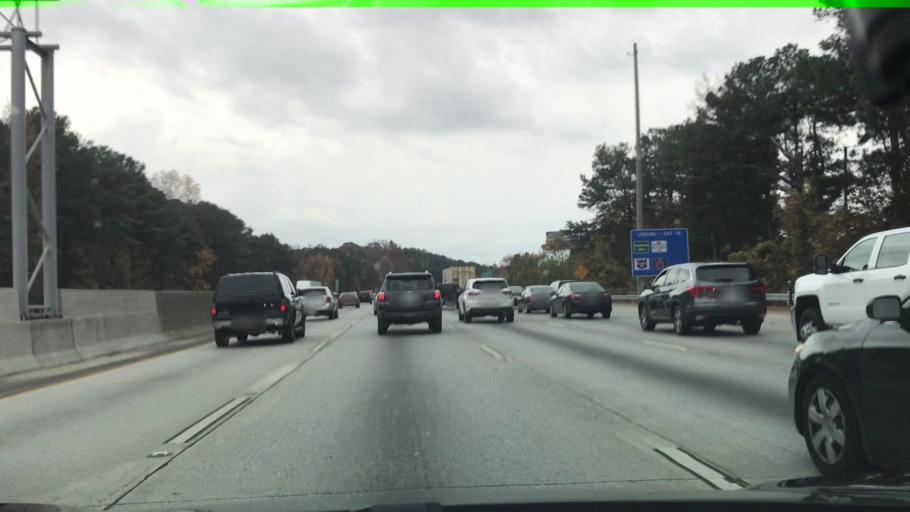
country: US
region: Georgia
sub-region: DeKalb County
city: Clarkston
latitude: 33.8415
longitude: -84.2479
